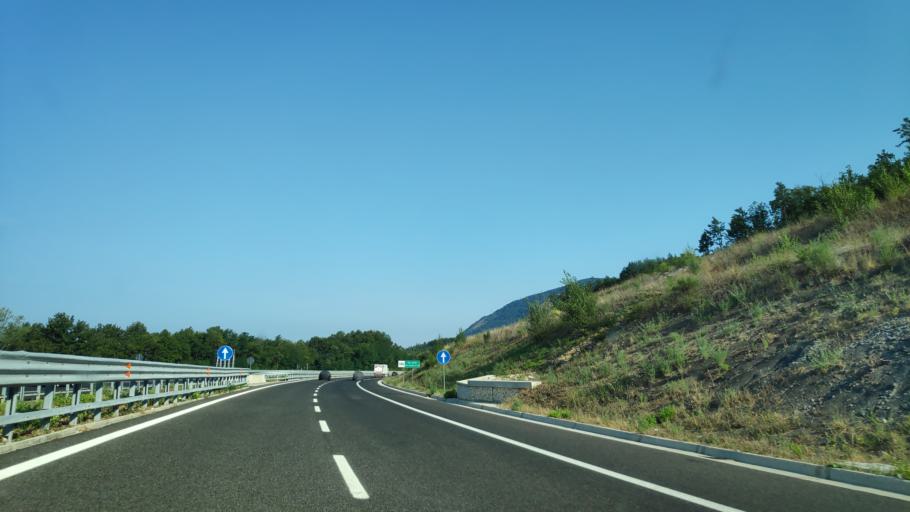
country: IT
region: Basilicate
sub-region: Provincia di Potenza
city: Nemoli
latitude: 40.1028
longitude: 15.7978
